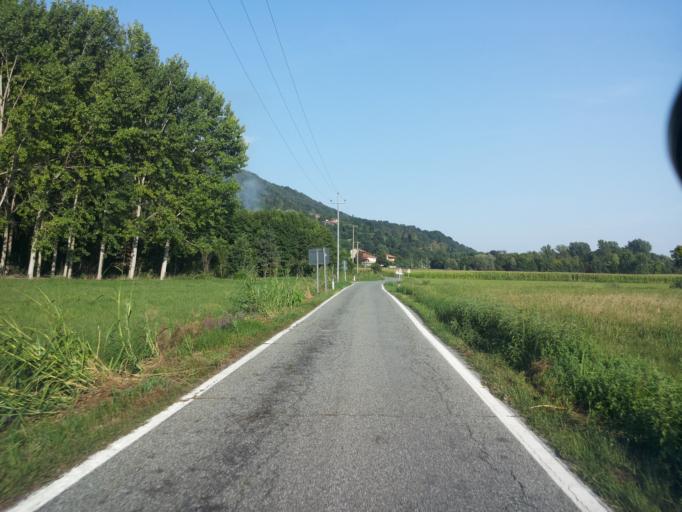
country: IT
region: Piedmont
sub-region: Provincia di Torino
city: Bollengo
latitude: 45.4698
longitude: 7.9522
